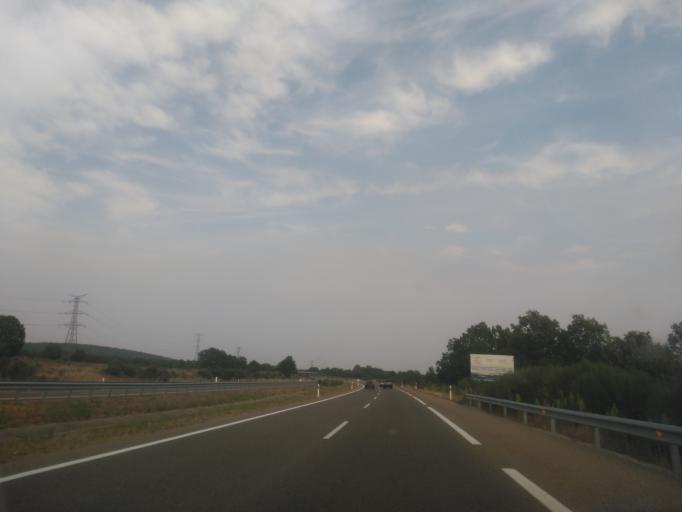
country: ES
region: Castille and Leon
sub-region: Provincia de Zamora
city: Cernadilla
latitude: 42.0235
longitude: -6.3986
